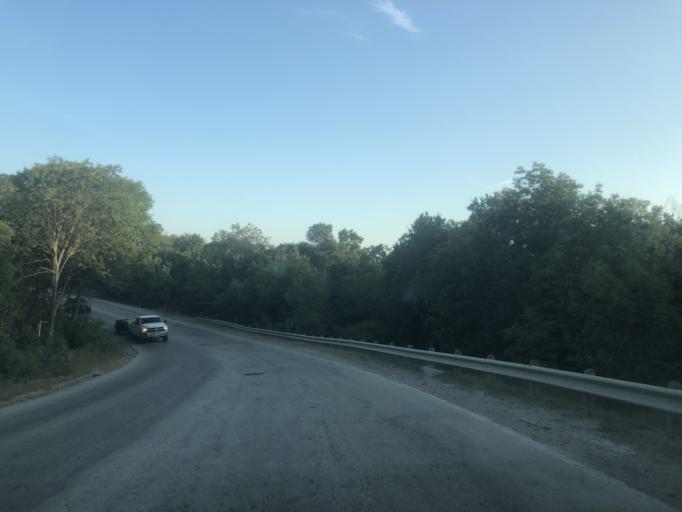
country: US
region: Texas
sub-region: Tarrant County
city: Lakeside
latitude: 32.7863
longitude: -97.4868
